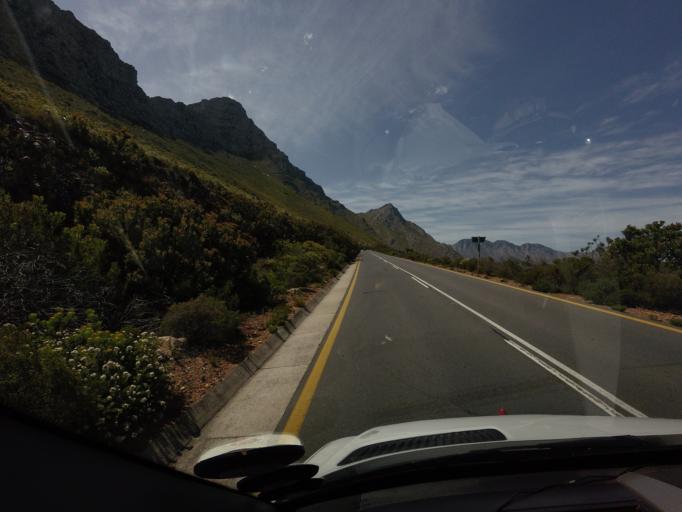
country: ZA
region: Western Cape
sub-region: Overberg District Municipality
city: Grabouw
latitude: -34.2000
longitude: 18.8269
